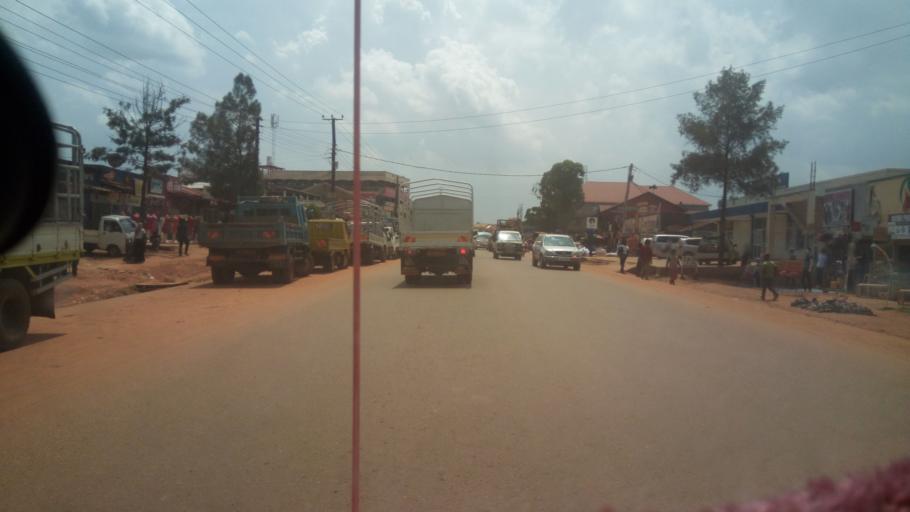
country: UG
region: Central Region
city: Kampala Central Division
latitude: 0.3660
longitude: 32.5256
